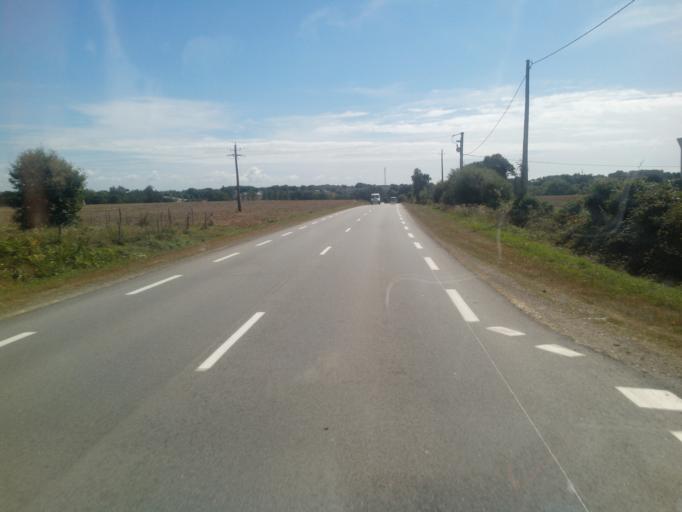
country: FR
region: Brittany
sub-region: Departement du Morbihan
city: Peaule
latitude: 47.5466
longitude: -2.3986
